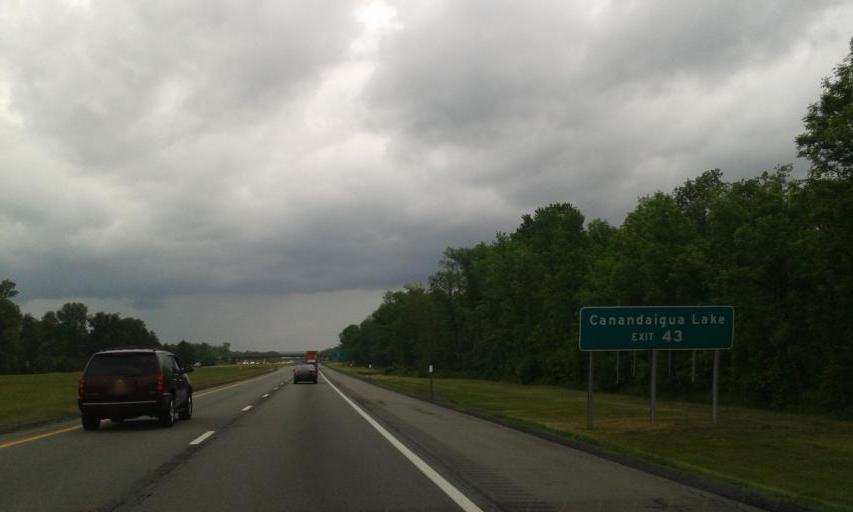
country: US
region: New York
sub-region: Ontario County
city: Manchester
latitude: 42.9783
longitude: -77.2181
